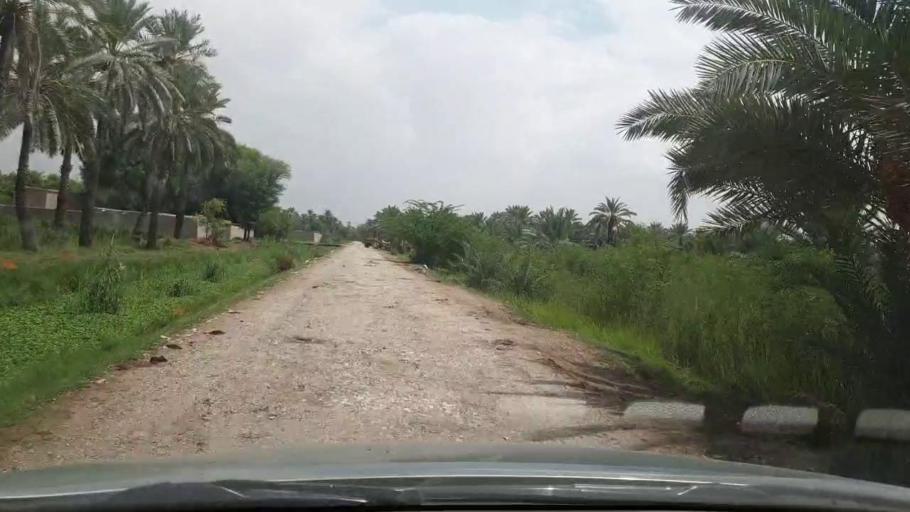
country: PK
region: Sindh
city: Kot Diji
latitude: 27.4126
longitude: 68.7605
